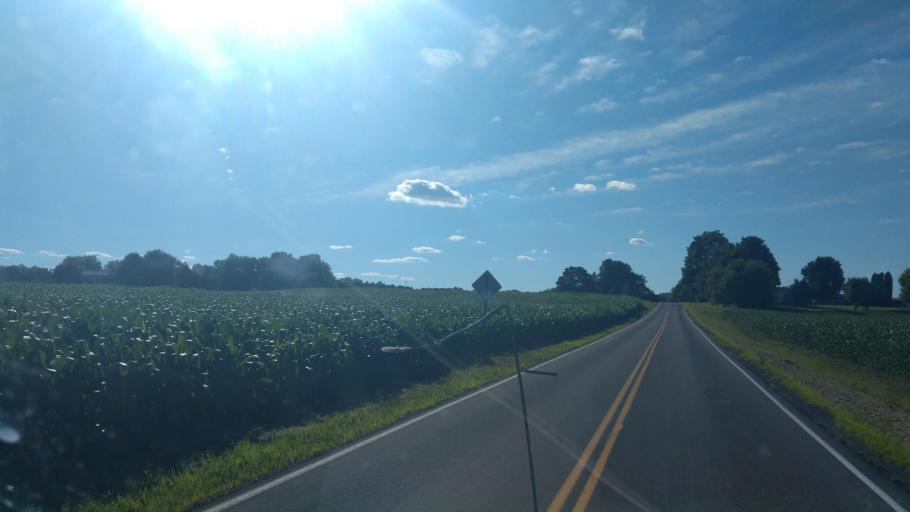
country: US
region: New York
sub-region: Wayne County
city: Lyons
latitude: 43.0009
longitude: -76.9595
